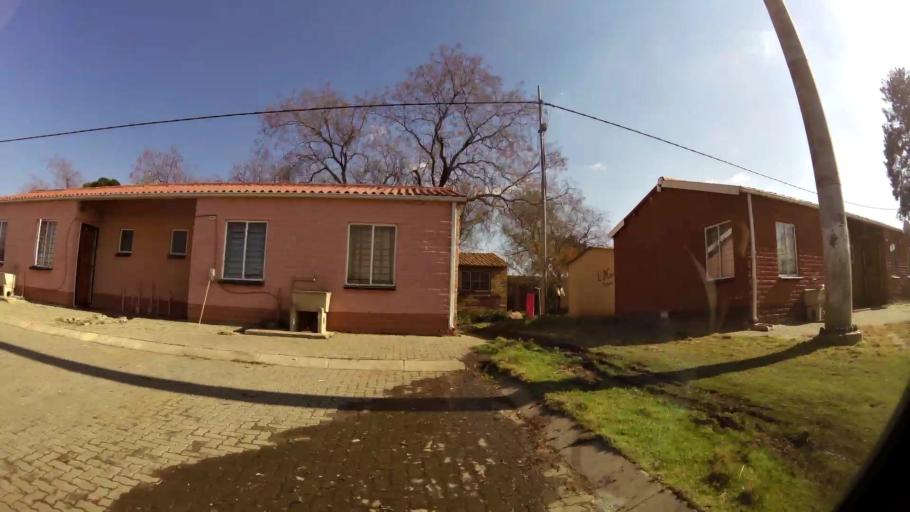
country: ZA
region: Gauteng
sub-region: City of Johannesburg Metropolitan Municipality
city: Soweto
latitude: -26.2241
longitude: 27.9266
